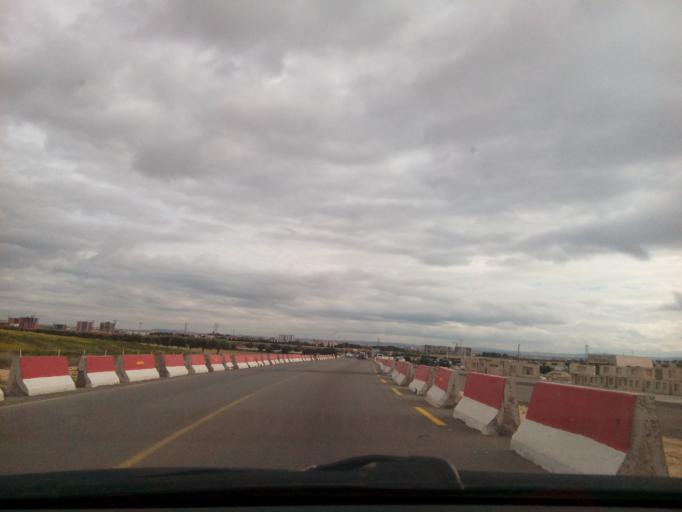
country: DZ
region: Sidi Bel Abbes
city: Sidi Bel Abbes
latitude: 35.2166
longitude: -0.6697
